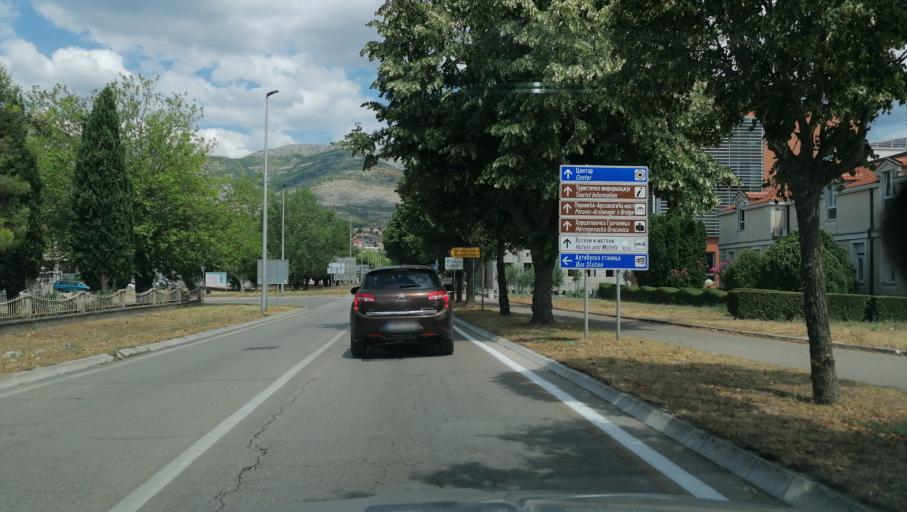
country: BA
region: Republika Srpska
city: Trebinje
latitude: 42.7063
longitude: 18.3428
